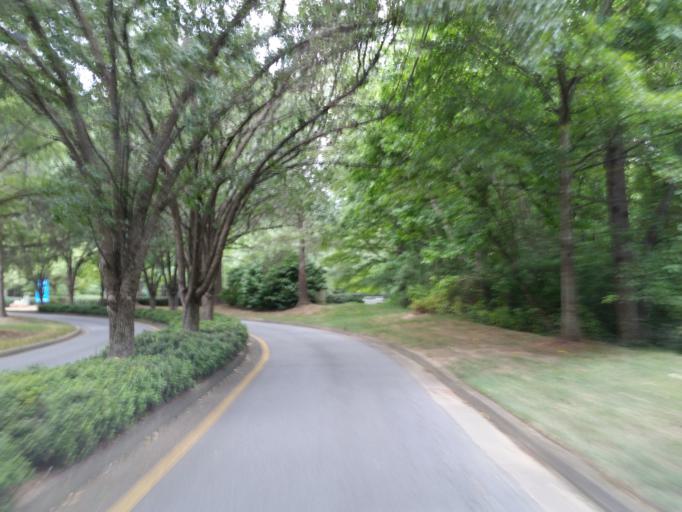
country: US
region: Georgia
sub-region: Cobb County
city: Smyrna
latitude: 33.9266
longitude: -84.4799
